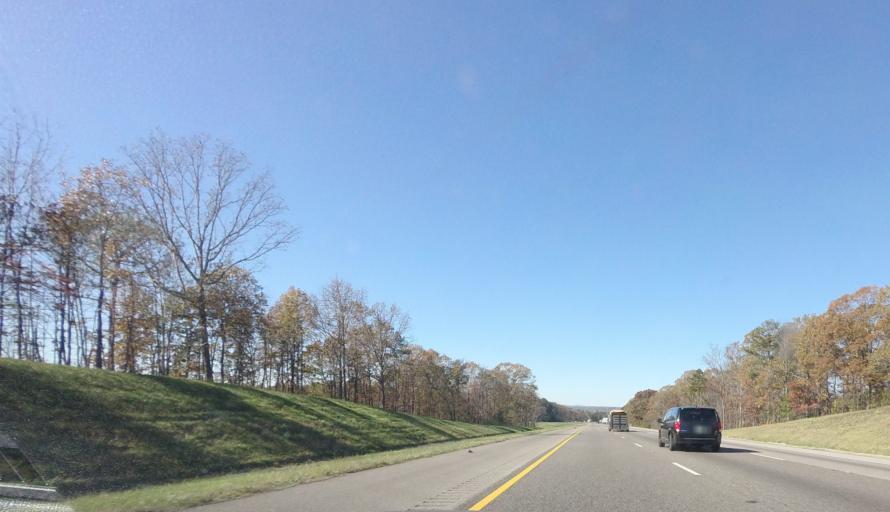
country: US
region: Alabama
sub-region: Calhoun County
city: Bynum
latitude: 33.5766
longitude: -85.9978
